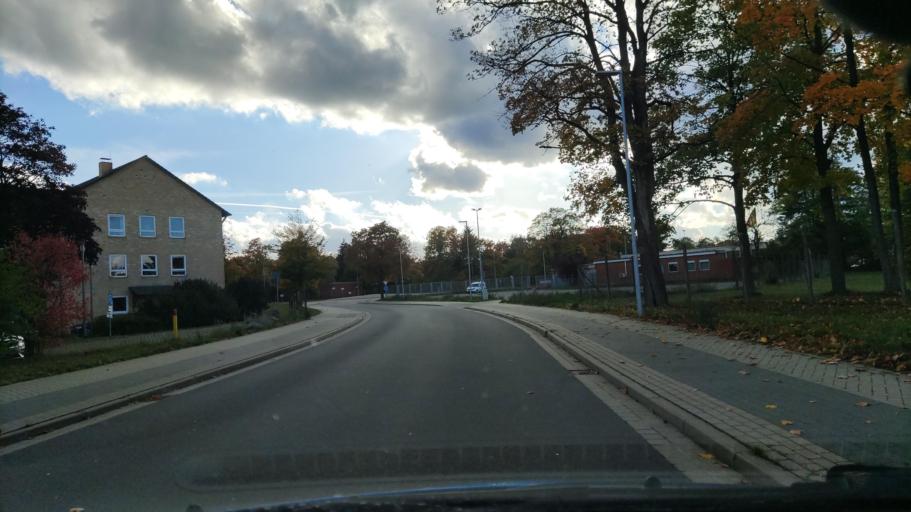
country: DE
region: Lower Saxony
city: Munster
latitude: 52.9865
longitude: 10.0759
